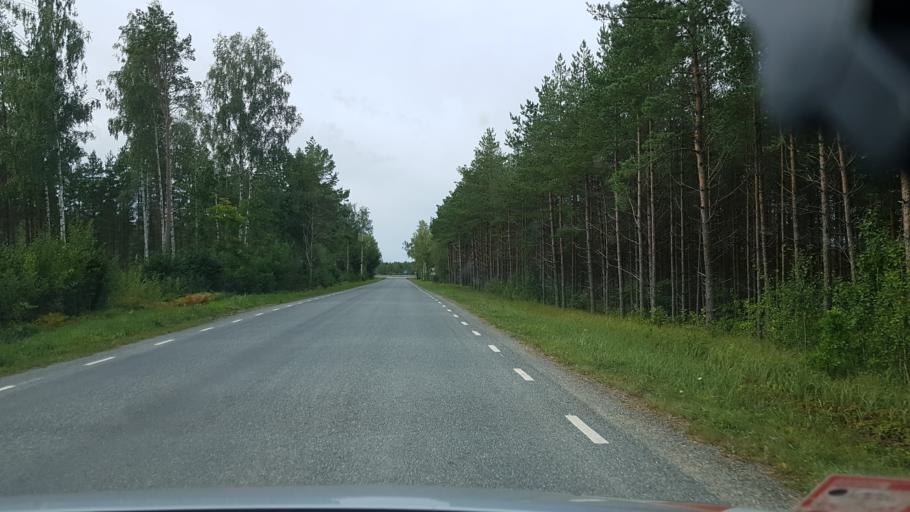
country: EE
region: Saare
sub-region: Kuressaare linn
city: Kuressaare
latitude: 58.4589
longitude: 22.7102
